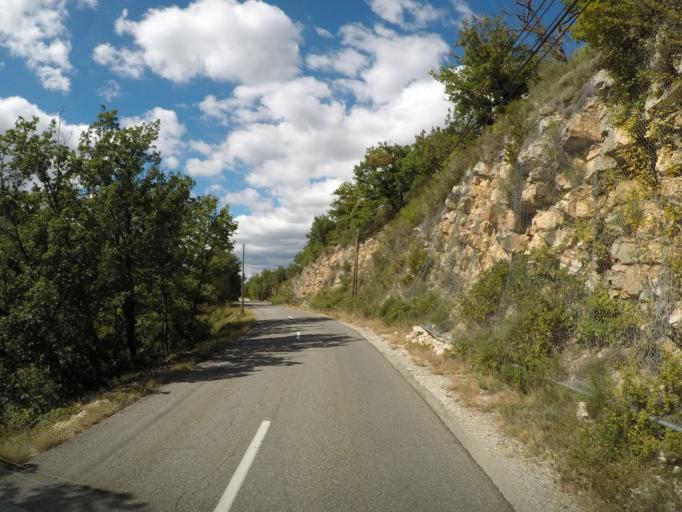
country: FR
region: Provence-Alpes-Cote d'Azur
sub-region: Departement des Hautes-Alpes
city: Laragne-Monteglin
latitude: 44.1732
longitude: 5.7251
